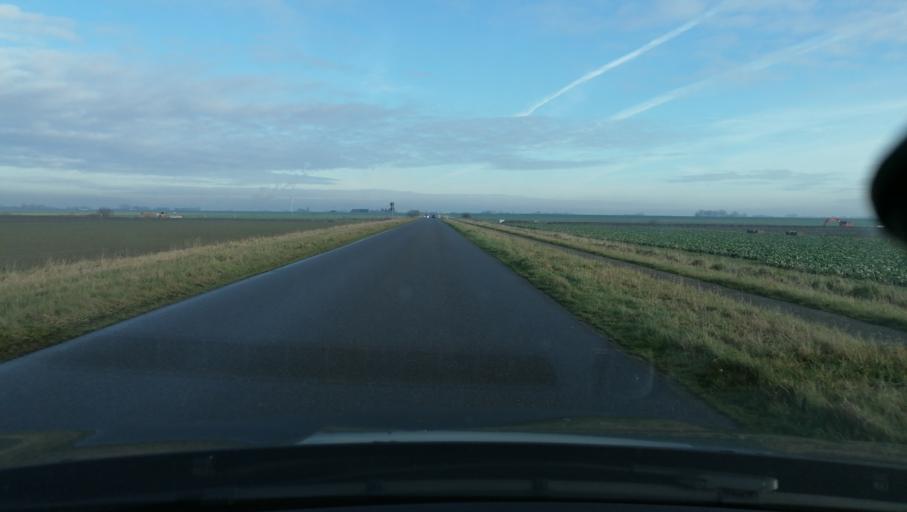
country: DE
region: Schleswig-Holstein
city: Friedrichsgabekoog
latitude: 54.1187
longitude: 8.9723
